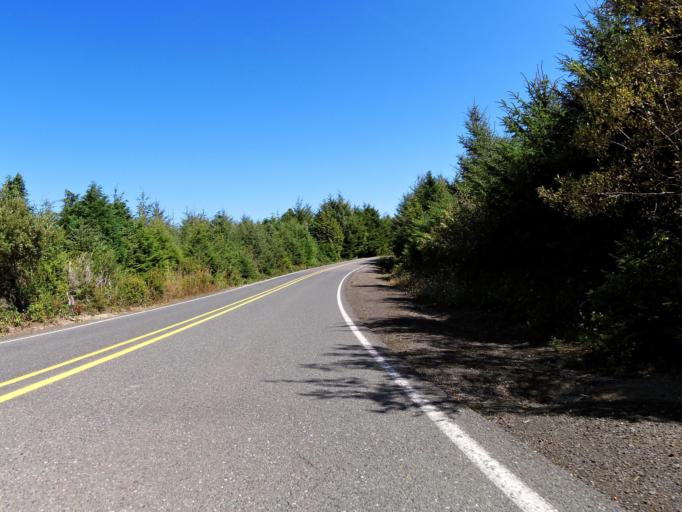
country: US
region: Oregon
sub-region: Coos County
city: Barview
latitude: 43.2711
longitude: -124.3502
